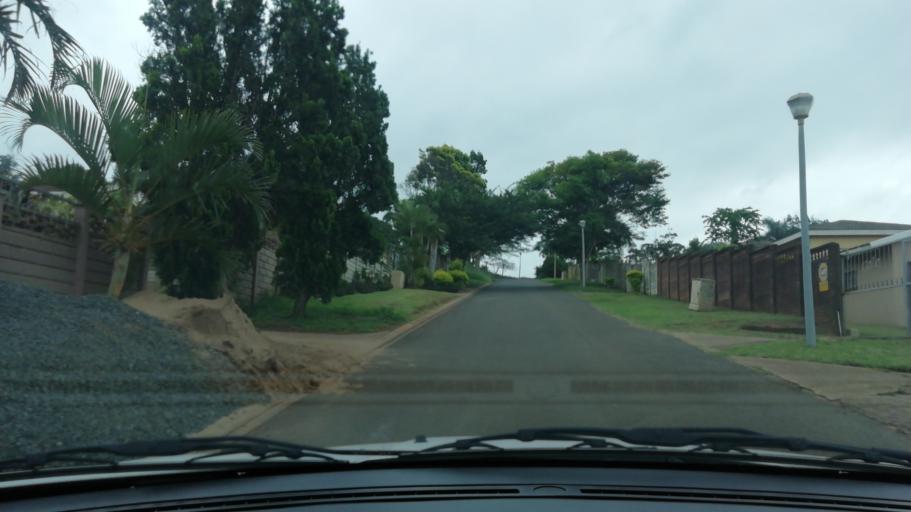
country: ZA
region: KwaZulu-Natal
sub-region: uThungulu District Municipality
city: Empangeni
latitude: -28.7613
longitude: 31.8832
